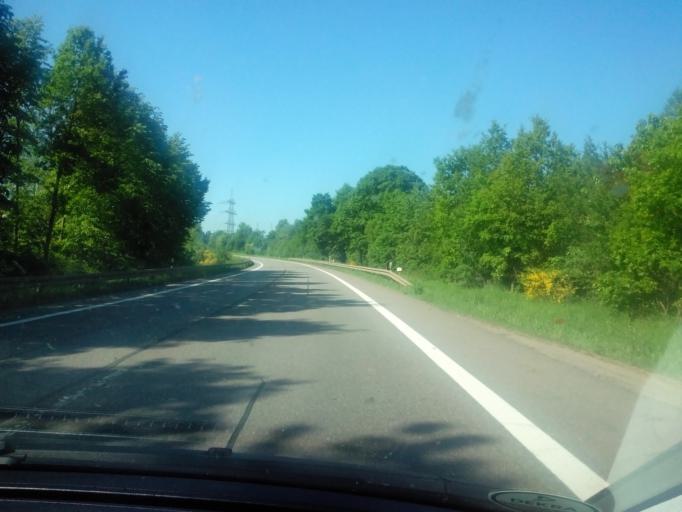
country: DE
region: Saarland
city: Nalbach
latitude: 49.3631
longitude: 6.7715
